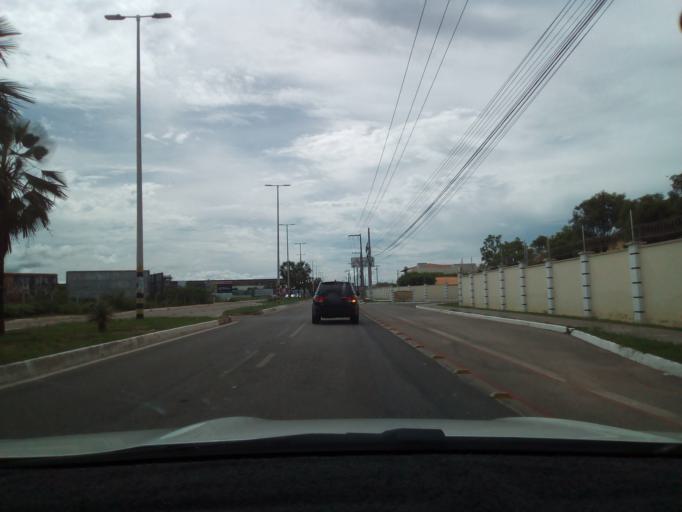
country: BR
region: Rio Grande do Norte
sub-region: Mossoro
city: Mossoro
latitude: -5.1738
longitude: -37.3720
